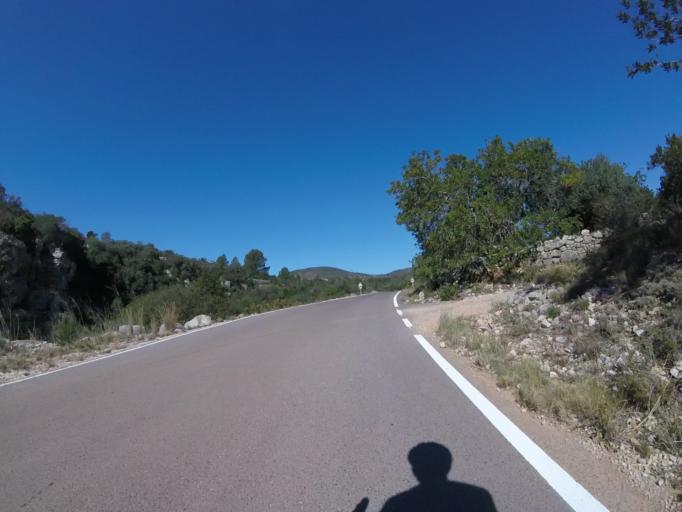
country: ES
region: Valencia
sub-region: Provincia de Castello
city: Santa Magdalena de Pulpis
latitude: 40.3719
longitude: 0.2731
